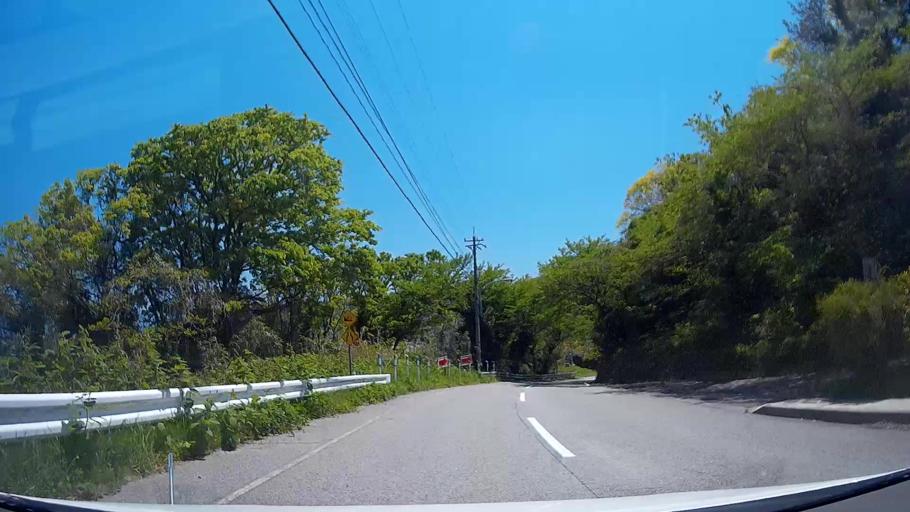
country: JP
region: Ishikawa
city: Nanao
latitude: 37.5297
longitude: 137.2757
